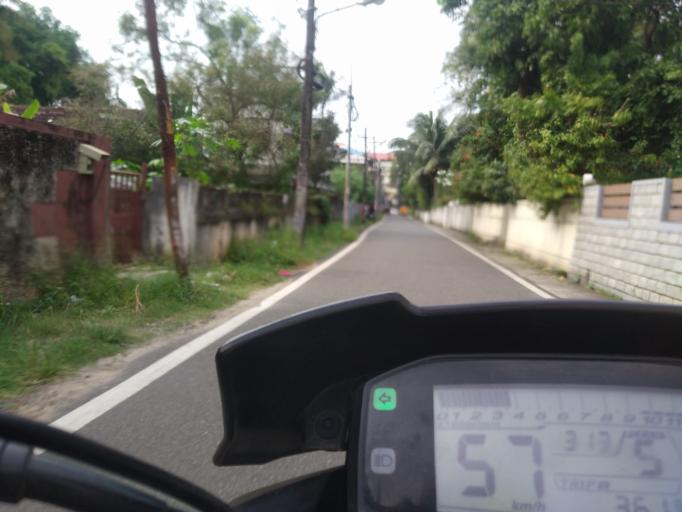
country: IN
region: Kerala
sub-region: Ernakulam
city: Cochin
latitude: 9.9750
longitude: 76.2870
